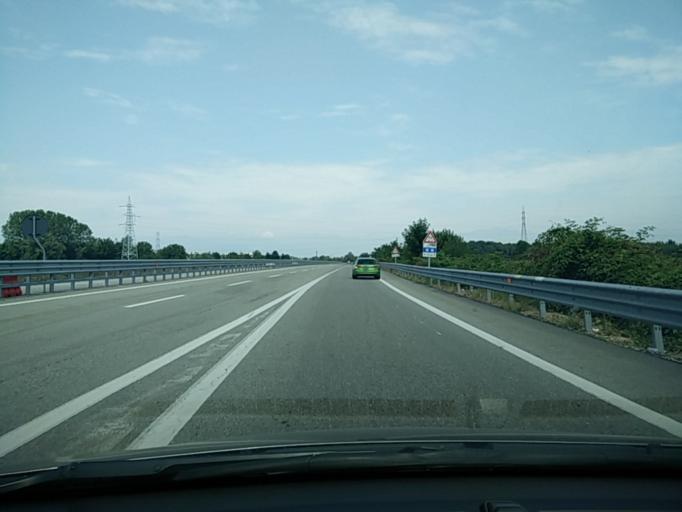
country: IT
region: Piedmont
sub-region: Provincia di Torino
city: Brandizzo
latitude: 45.1735
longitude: 7.8064
